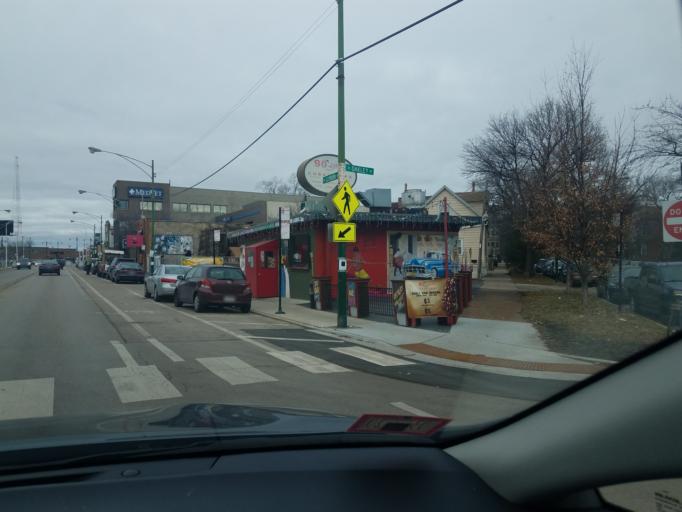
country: US
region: Illinois
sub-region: Cook County
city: Lincolnwood
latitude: 41.9378
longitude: -87.6857
